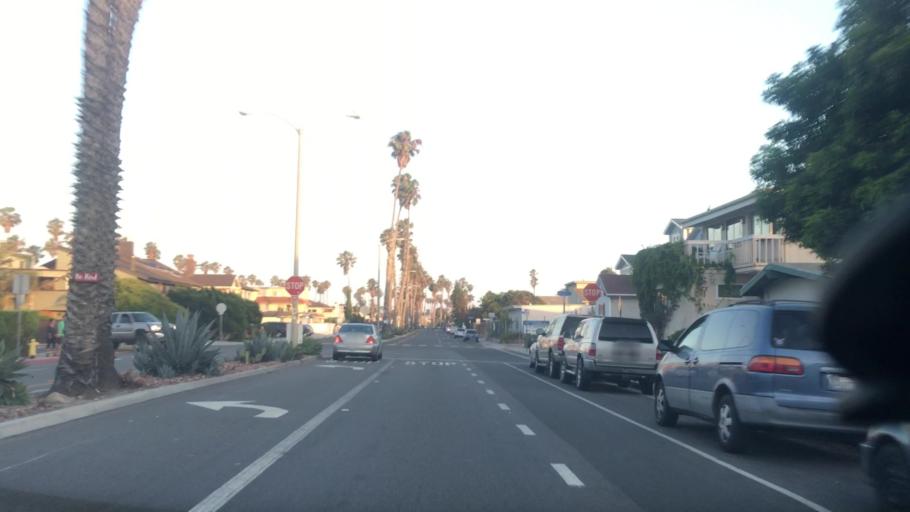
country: US
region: California
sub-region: Ventura County
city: Ventura
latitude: 34.2603
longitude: -119.2697
